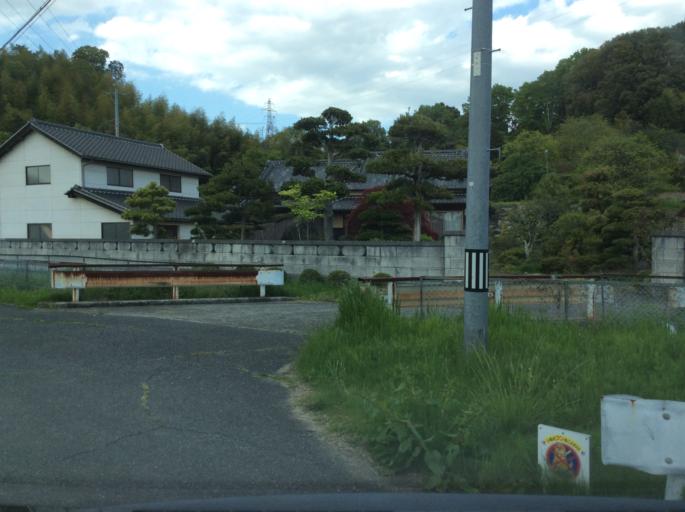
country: JP
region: Fukushima
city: Iwaki
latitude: 36.9603
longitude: 140.8561
